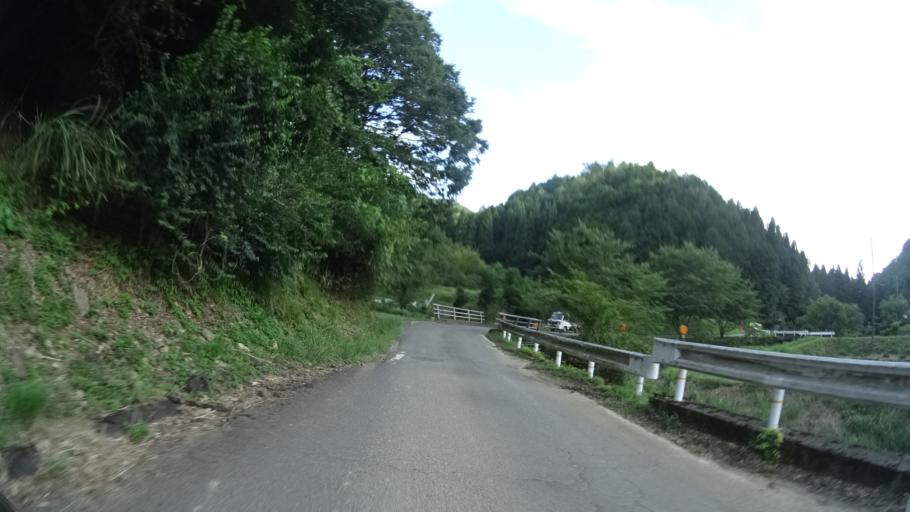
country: JP
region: Kyoto
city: Maizuru
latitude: 35.4015
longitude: 135.3497
